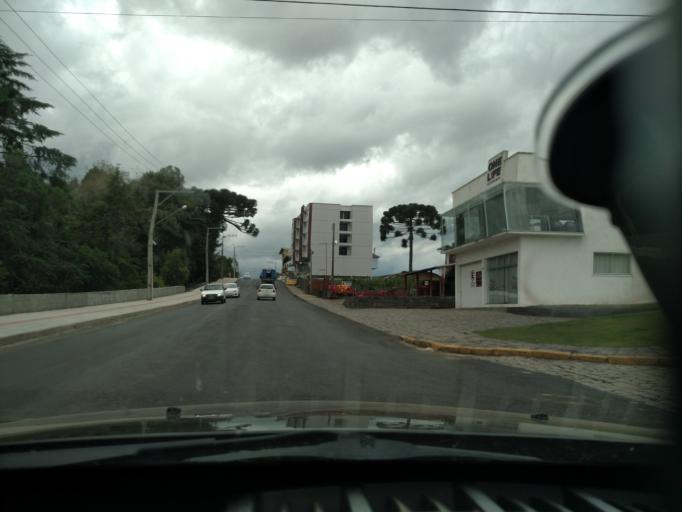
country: BR
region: Santa Catarina
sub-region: Sao Joaquim
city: Sao Joaquim
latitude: -28.2896
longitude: -49.9352
